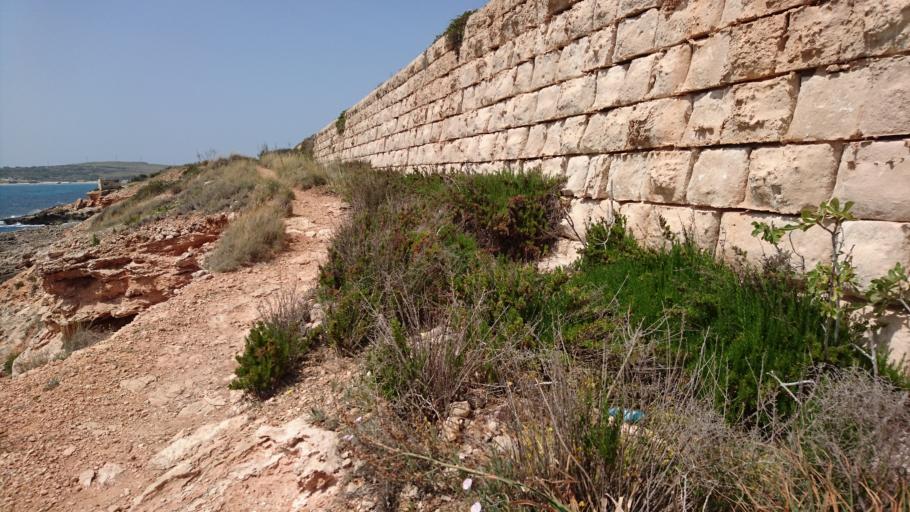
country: MT
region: Il-Mellieha
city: Mellieha
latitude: 35.9784
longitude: 14.3582
